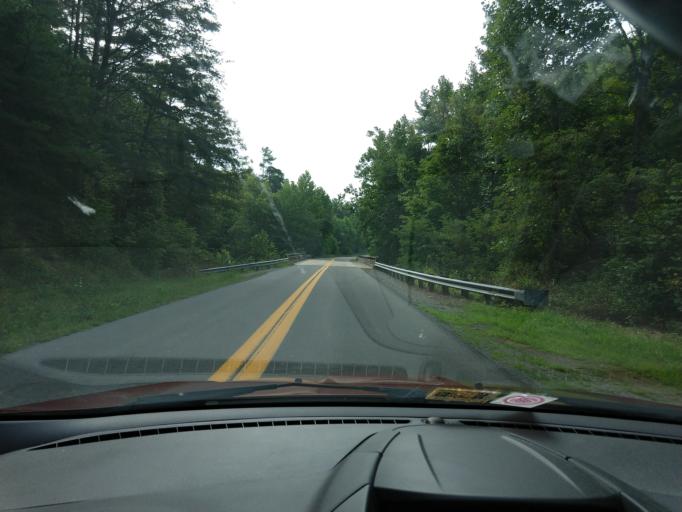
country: US
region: Virginia
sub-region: City of Covington
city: Covington
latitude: 37.9580
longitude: -80.1209
